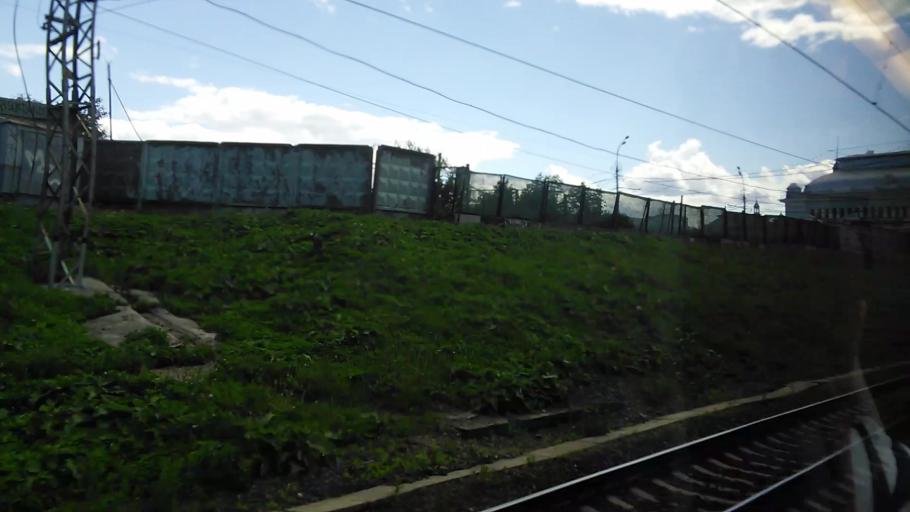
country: RU
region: Moskovskaya
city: Dorogomilovo
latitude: 55.7784
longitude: 37.5837
